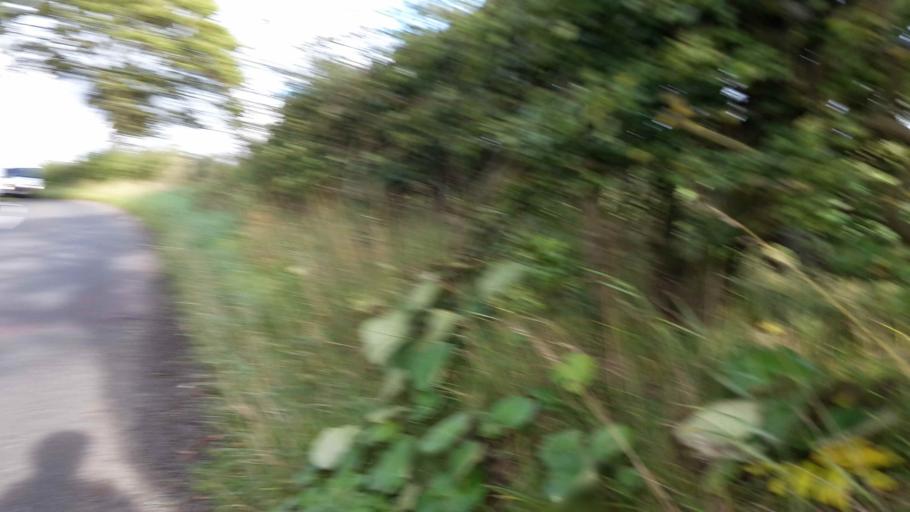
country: GB
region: Scotland
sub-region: South Lanarkshire
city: Carluke
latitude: 55.7181
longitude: -3.8238
